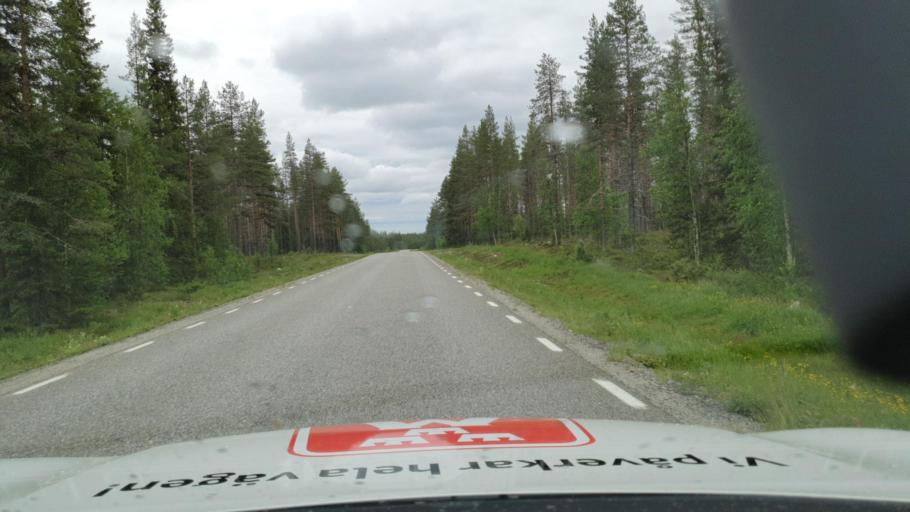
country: SE
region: Vaesterbotten
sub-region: Lycksele Kommun
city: Lycksele
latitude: 64.2621
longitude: 18.2073
